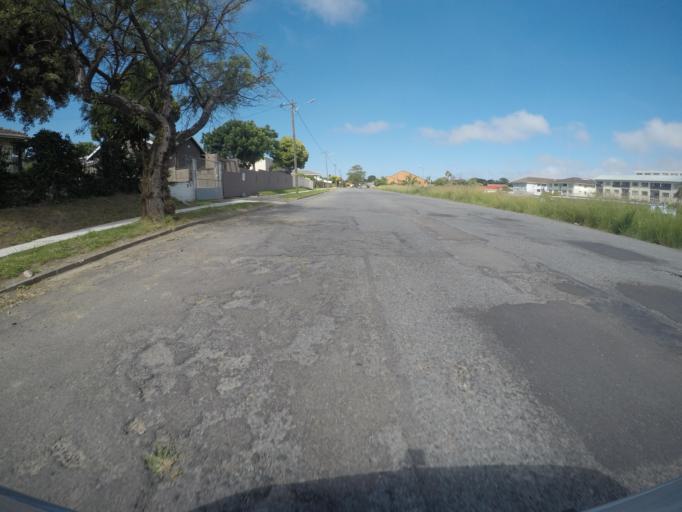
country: ZA
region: Eastern Cape
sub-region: Buffalo City Metropolitan Municipality
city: East London
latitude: -32.9823
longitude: 27.8937
